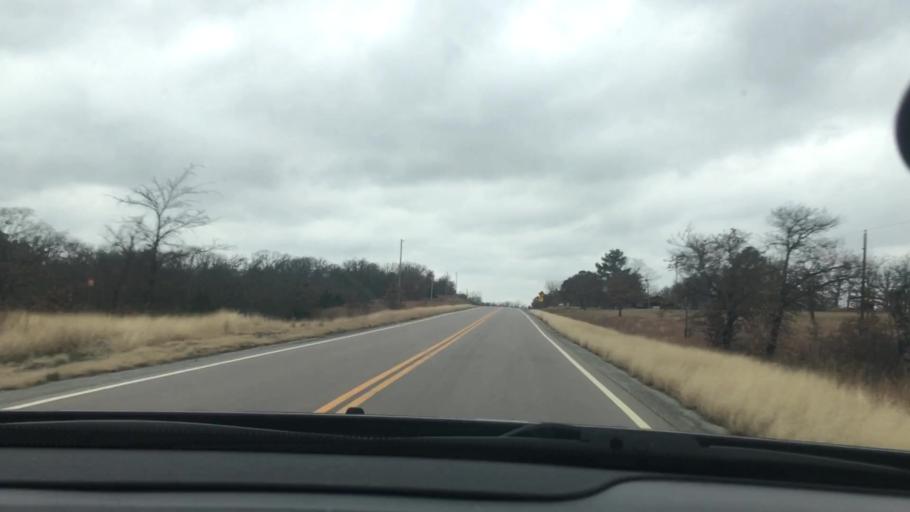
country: US
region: Oklahoma
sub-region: Coal County
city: Coalgate
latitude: 34.3728
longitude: -96.3739
